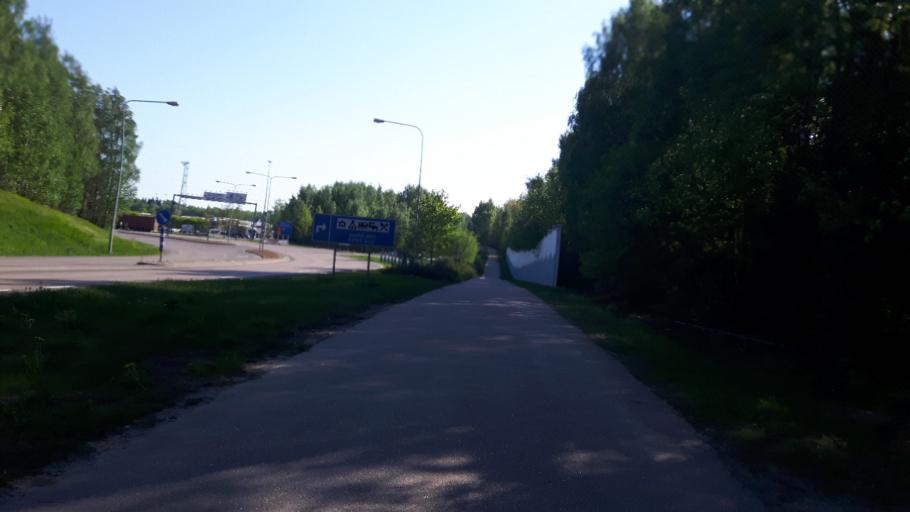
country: FI
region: Kymenlaakso
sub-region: Kotka-Hamina
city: Kotka
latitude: 60.4405
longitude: 26.8849
